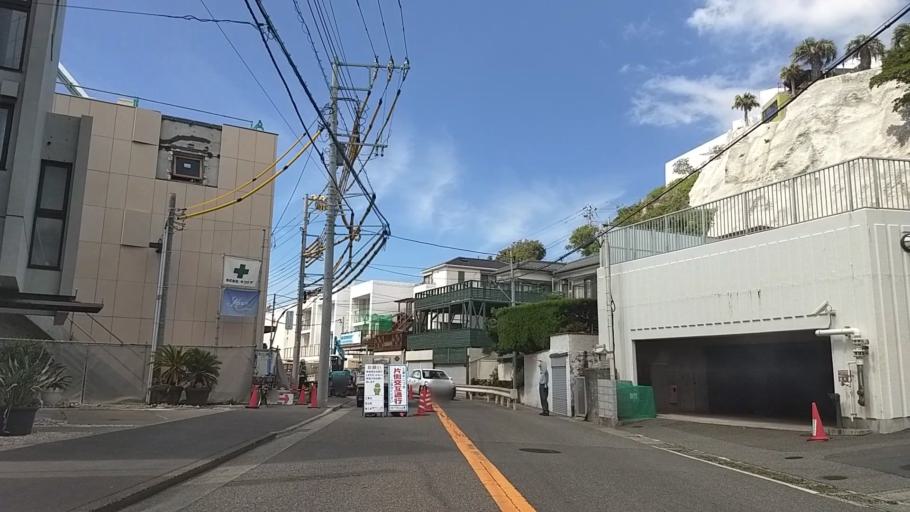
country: JP
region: Kanagawa
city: Hayama
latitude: 35.2273
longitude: 139.6040
